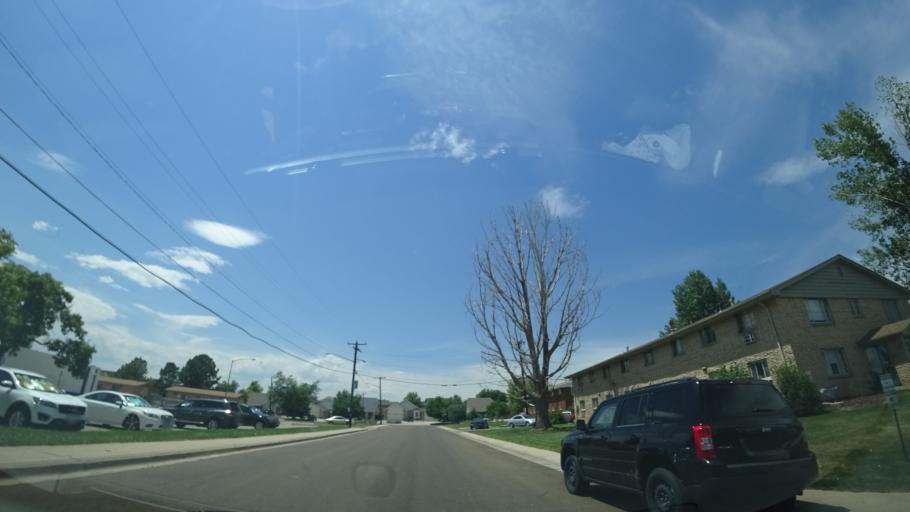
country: US
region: Colorado
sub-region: Jefferson County
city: Lakewood
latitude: 39.6947
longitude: -105.0851
